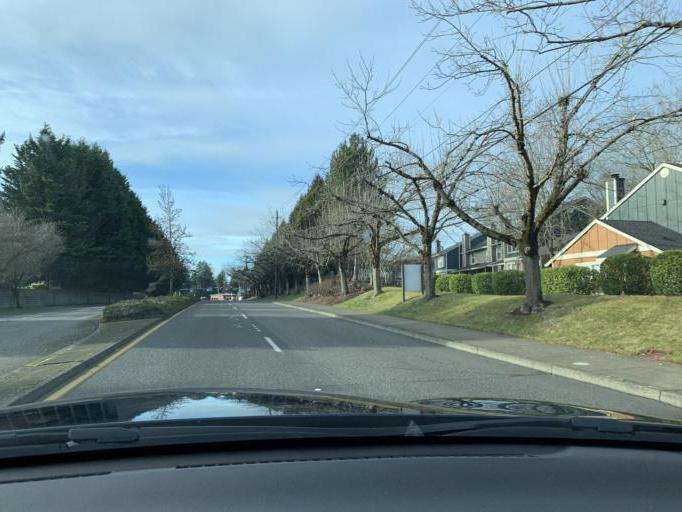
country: US
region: Washington
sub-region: Clark County
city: Mill Plain
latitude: 45.5968
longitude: -122.5006
